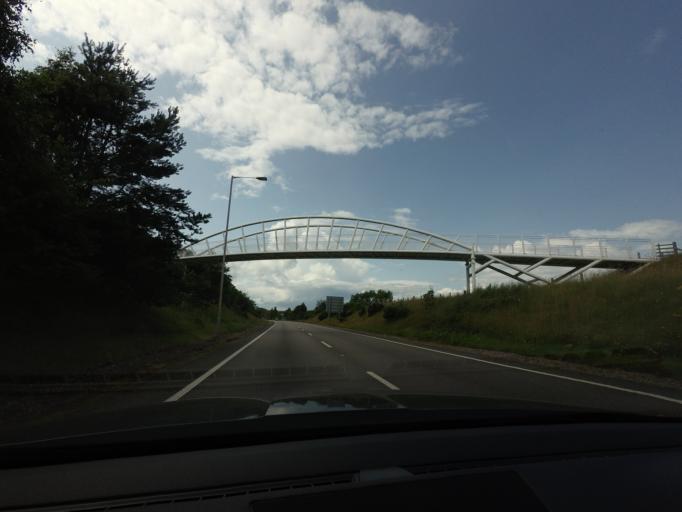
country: GB
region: Scotland
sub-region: Moray
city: Forres
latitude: 57.6161
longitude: -3.5974
